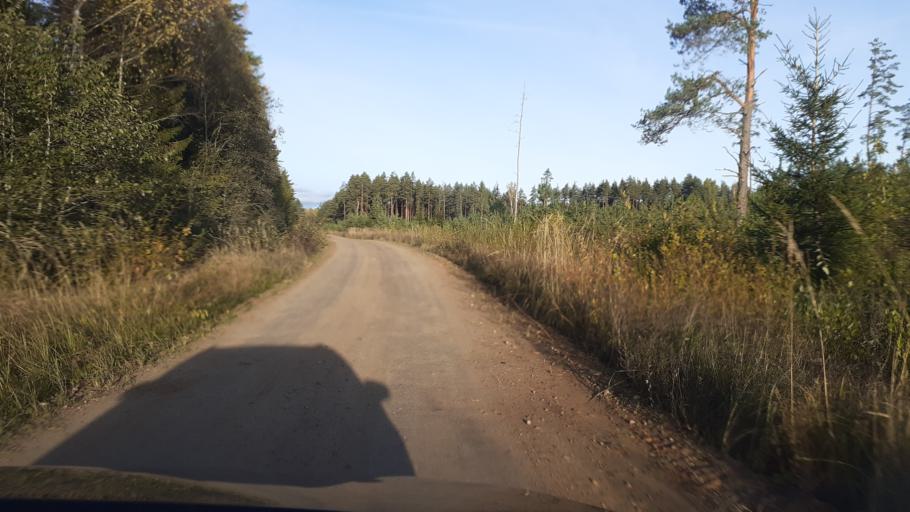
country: LV
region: Kuldigas Rajons
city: Kuldiga
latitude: 56.8614
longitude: 22.1027
